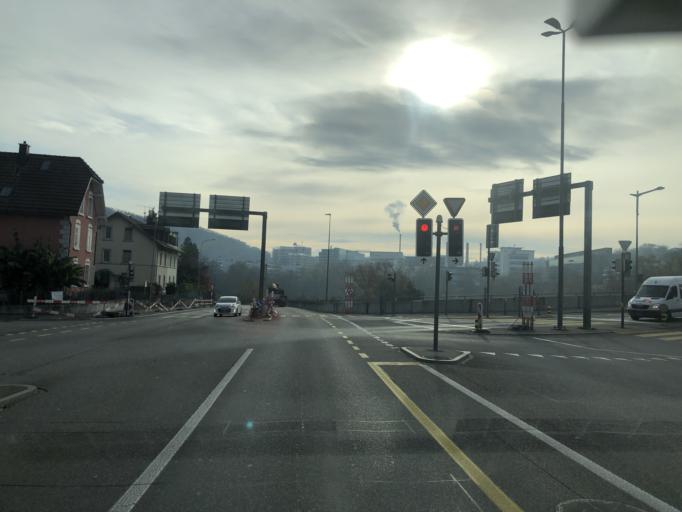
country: CH
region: Aargau
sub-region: Bezirk Baden
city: Obersiggenthal
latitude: 47.4849
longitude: 8.2995
